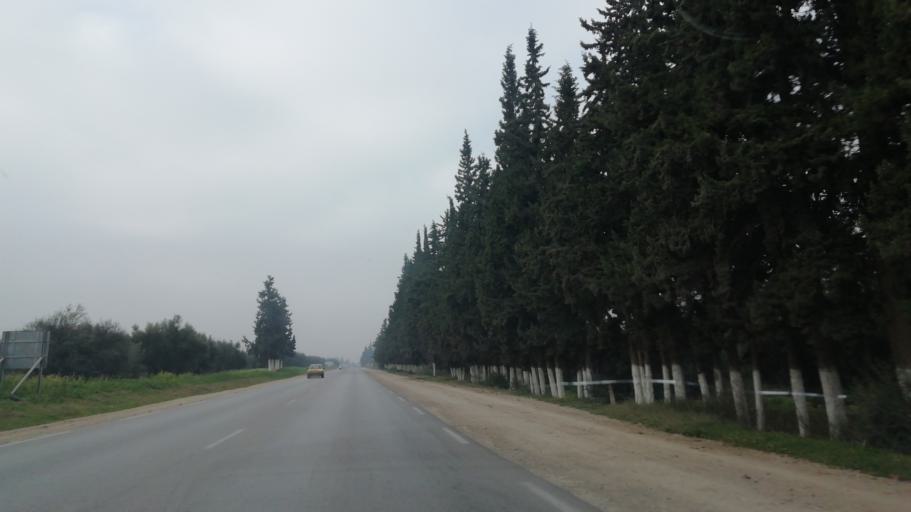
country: DZ
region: Relizane
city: Djidiouia
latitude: 35.9465
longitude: 0.8709
